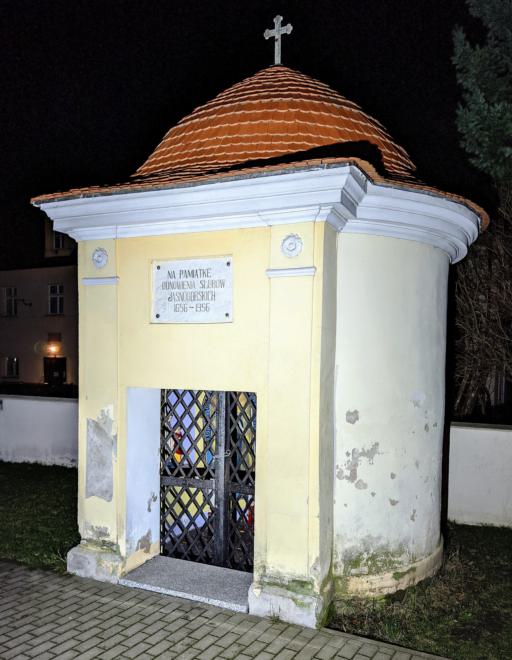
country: PL
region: Lower Silesian Voivodeship
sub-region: Powiat polkowicki
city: Przemkow
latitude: 51.5271
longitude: 15.7857
